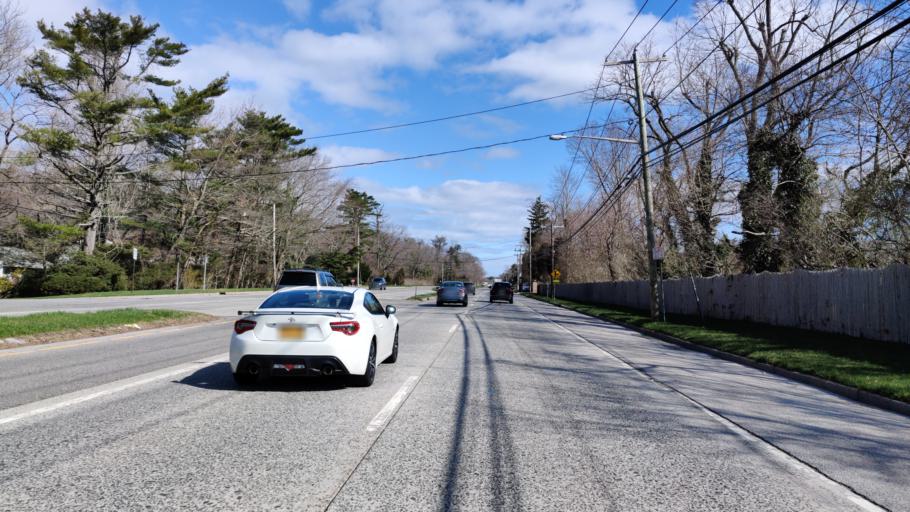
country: US
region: New York
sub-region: Suffolk County
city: Dix Hills
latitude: 40.8059
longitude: -73.3424
